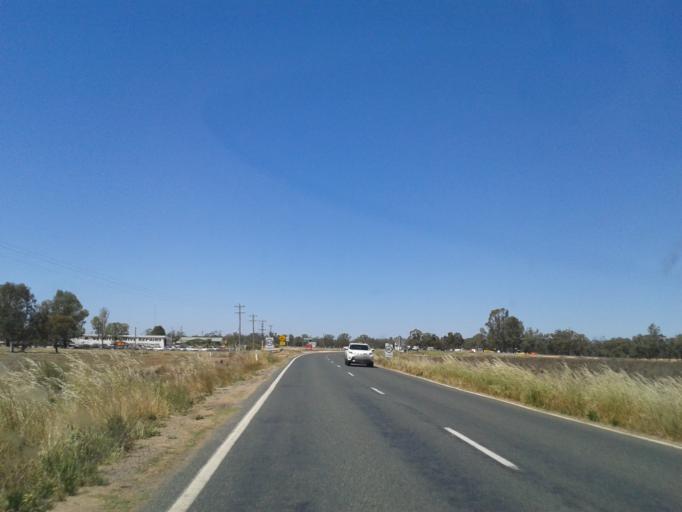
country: AU
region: New South Wales
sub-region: Wentworth
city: Gol Gol
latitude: -34.5582
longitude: 142.7585
